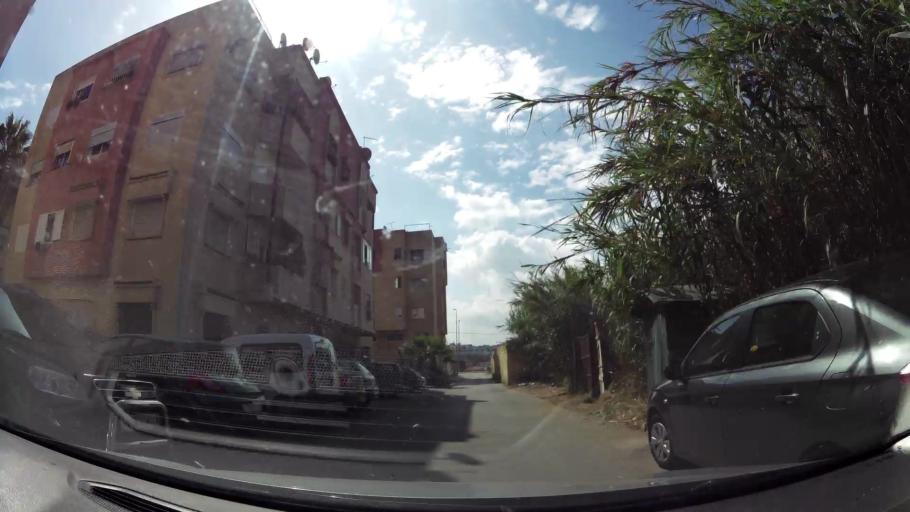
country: MA
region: Rabat-Sale-Zemmour-Zaer
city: Sale
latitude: 34.0612
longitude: -6.8025
